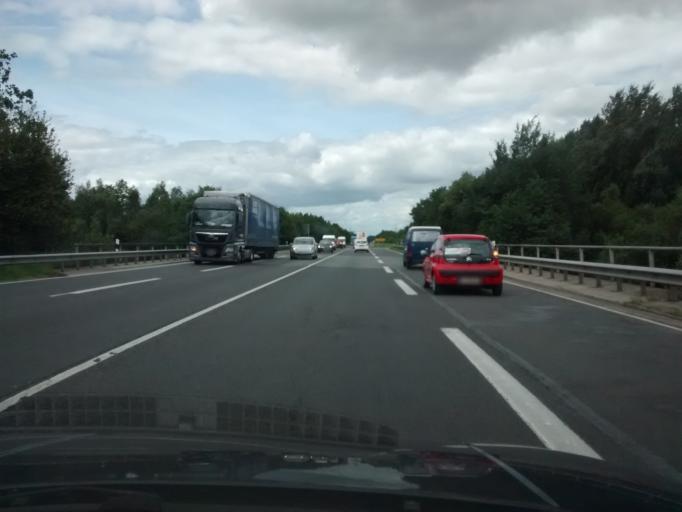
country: DE
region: Lower Saxony
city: Cappeln
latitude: 52.8286
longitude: 8.1221
